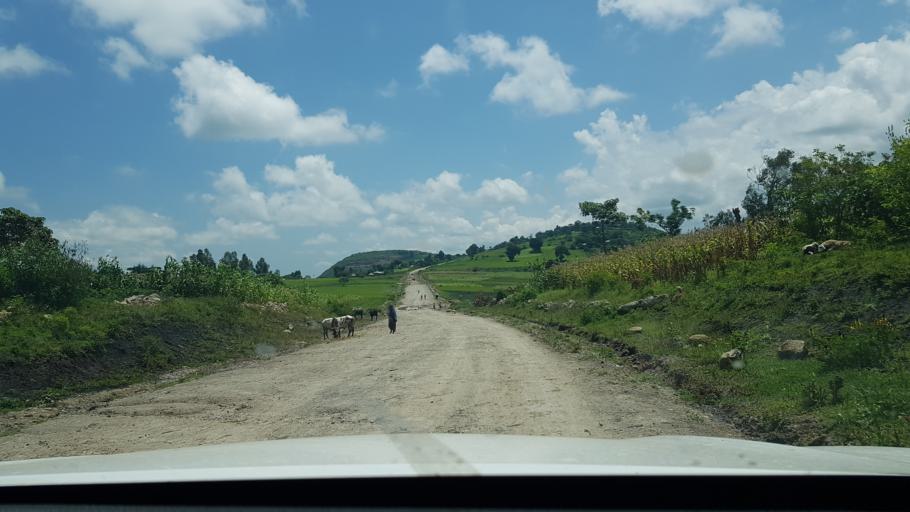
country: ET
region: Oromiya
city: Sirre
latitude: 8.4367
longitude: 39.8766
